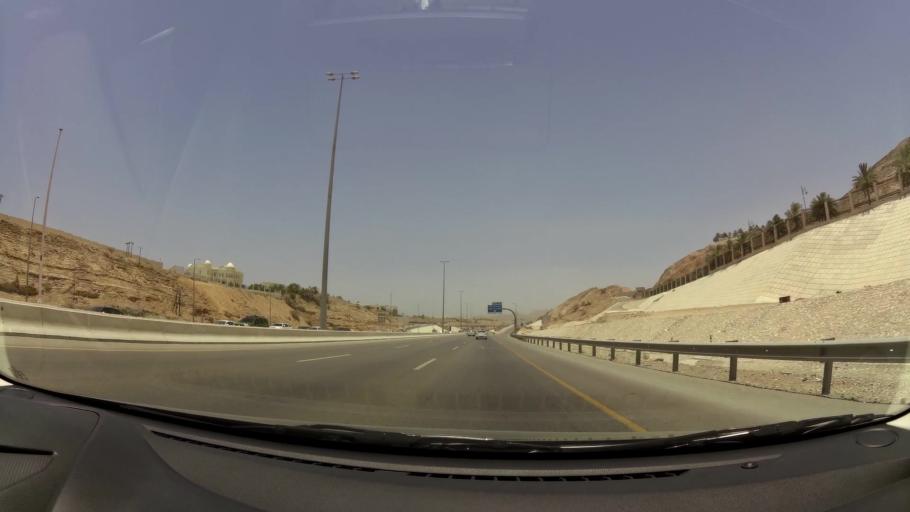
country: OM
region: Muhafazat Masqat
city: Bawshar
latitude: 23.5947
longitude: 58.4736
